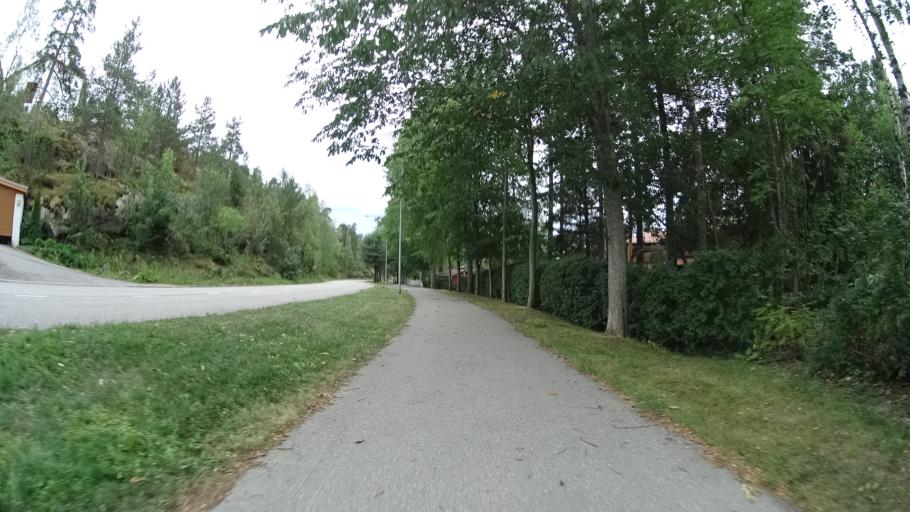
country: FI
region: Uusimaa
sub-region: Helsinki
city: Espoo
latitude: 60.1339
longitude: 24.6663
